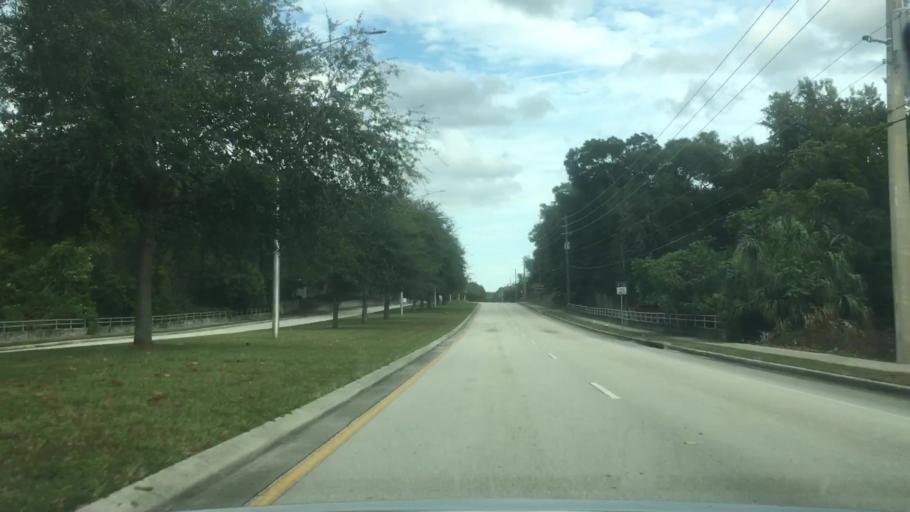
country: US
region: Florida
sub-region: Duval County
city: Atlantic Beach
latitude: 30.3498
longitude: -81.5182
